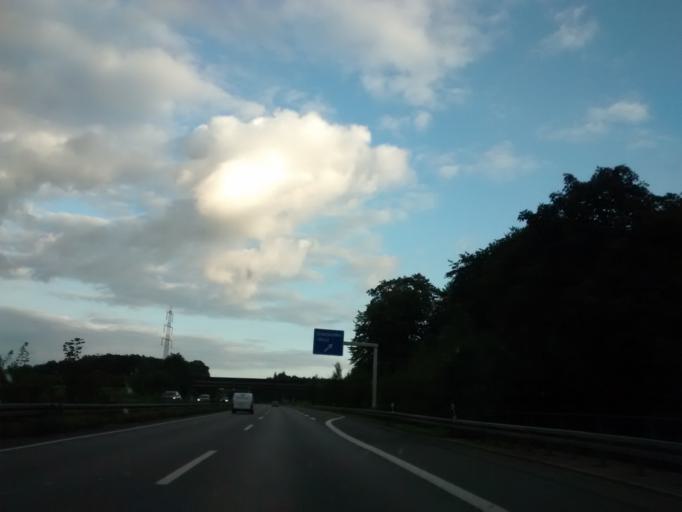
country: DE
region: North Rhine-Westphalia
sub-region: Regierungsbezirk Munster
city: Birgte
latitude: 52.2720
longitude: 7.6542
